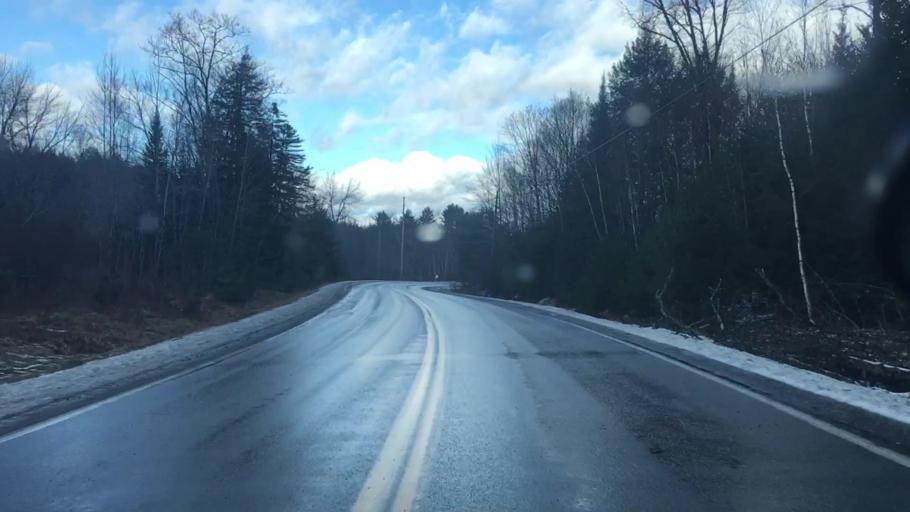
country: US
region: Maine
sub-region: Hancock County
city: Dedham
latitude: 44.6451
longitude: -68.6918
